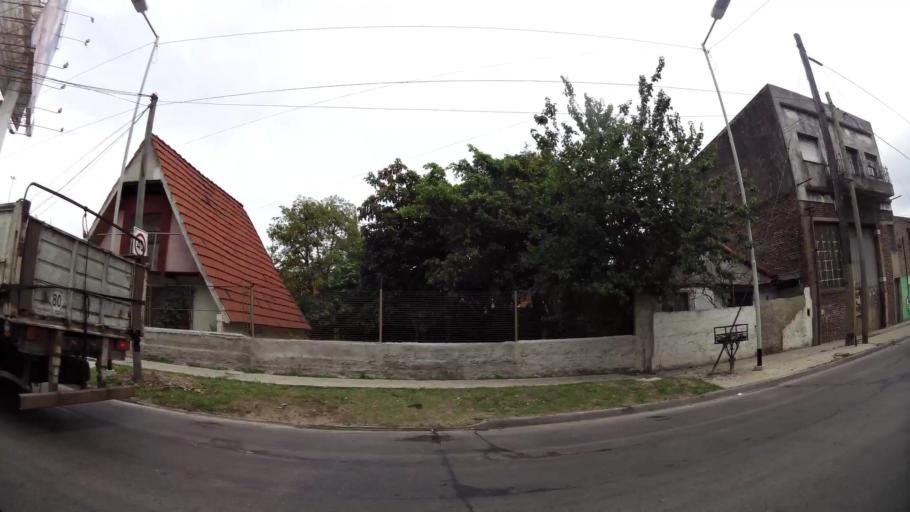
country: AR
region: Buenos Aires
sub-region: Partido de Avellaneda
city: Avellaneda
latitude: -34.6591
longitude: -58.3481
